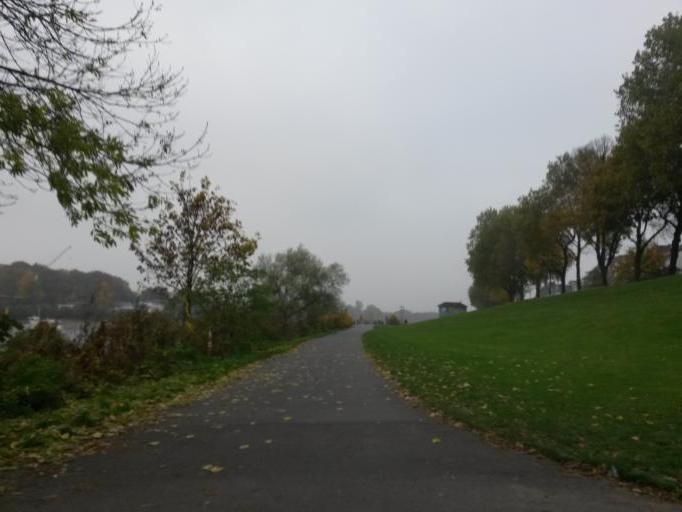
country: DE
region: Bremen
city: Bremen
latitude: 53.0686
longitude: 8.8246
